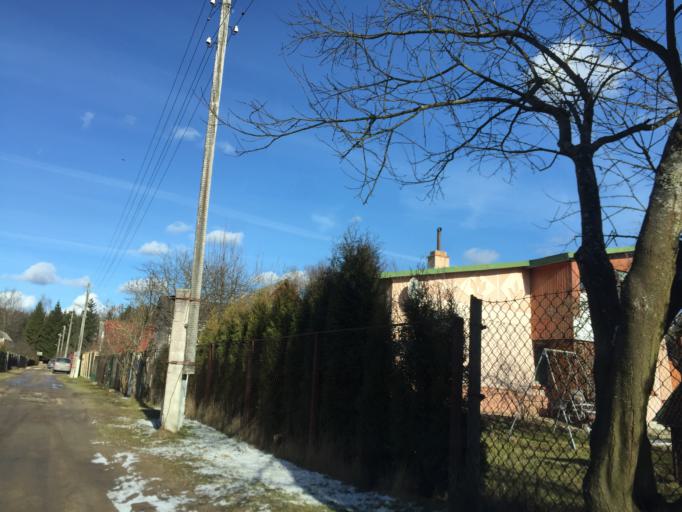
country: LV
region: Garkalne
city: Garkalne
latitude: 56.9494
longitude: 24.4520
